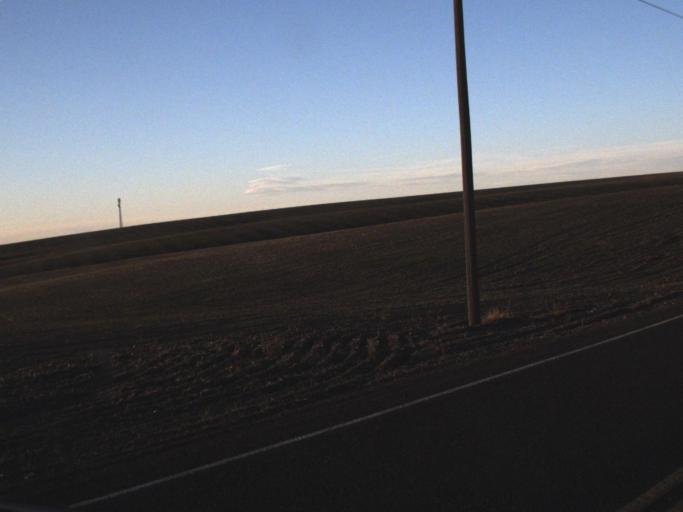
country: US
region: Washington
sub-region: Adams County
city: Ritzville
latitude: 46.9308
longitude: -118.5671
